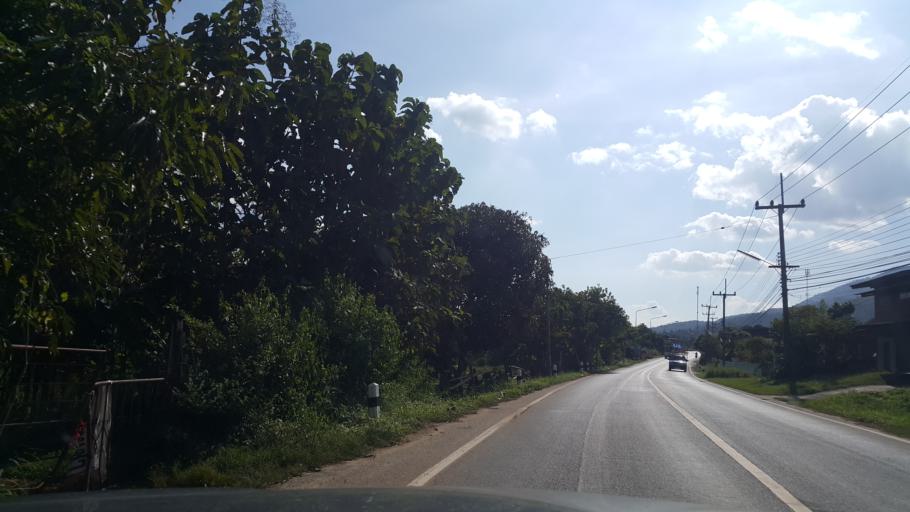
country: TH
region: Lamphun
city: Mae Tha
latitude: 18.5550
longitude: 99.2506
